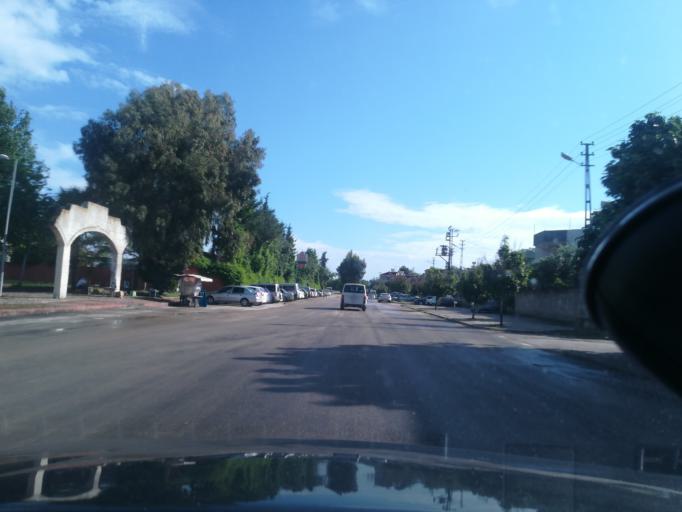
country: TR
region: Adana
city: Adana
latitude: 37.0227
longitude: 35.3633
